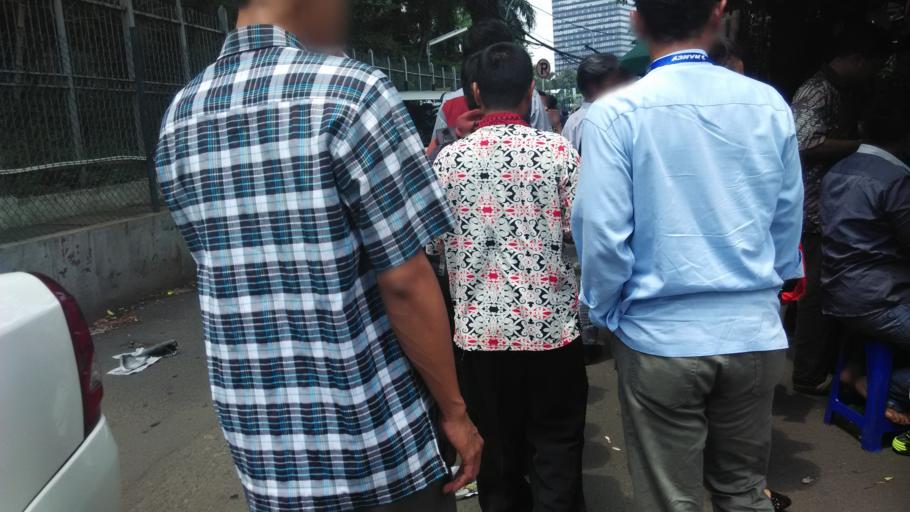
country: ID
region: Jakarta Raya
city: Jakarta
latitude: -6.2046
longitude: 106.8188
